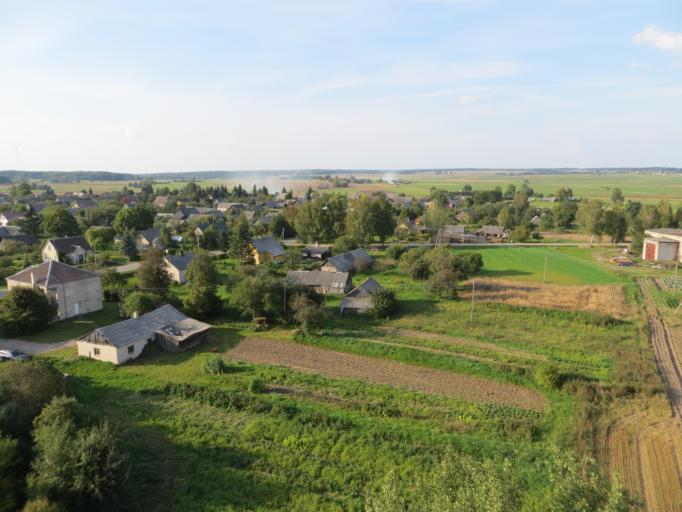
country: LT
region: Alytaus apskritis
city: Varena
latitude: 54.1182
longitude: 24.7590
